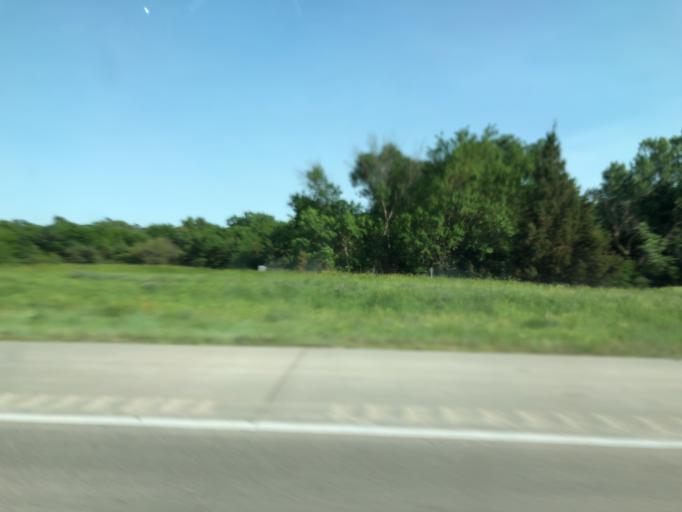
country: US
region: Nebraska
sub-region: Saunders County
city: Ashland
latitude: 40.9994
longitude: -96.3325
